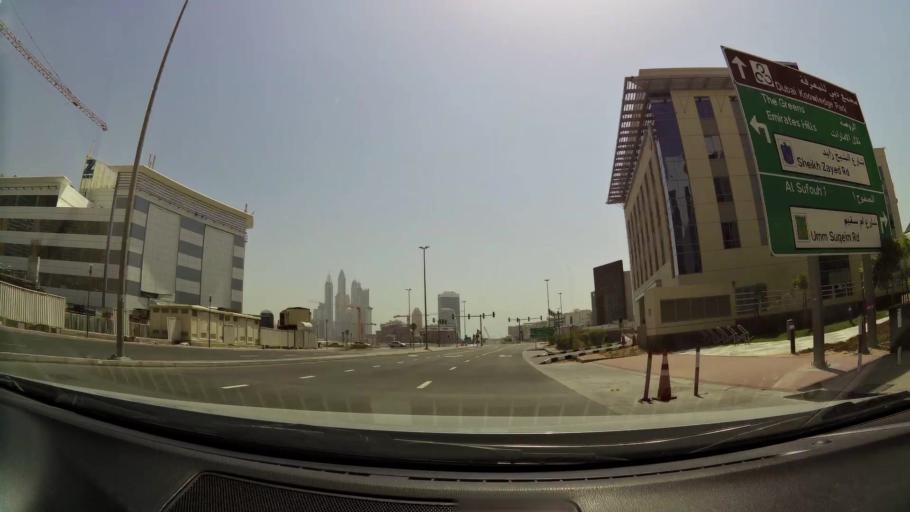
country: AE
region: Dubai
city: Dubai
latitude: 25.1029
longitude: 55.1686
